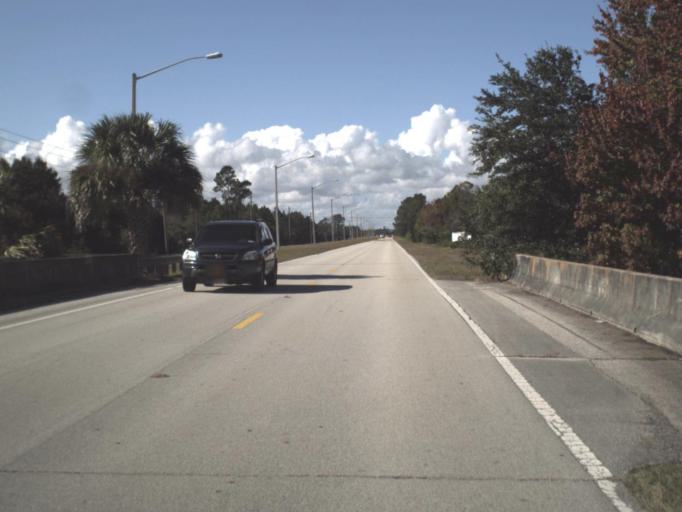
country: US
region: Florida
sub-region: Flagler County
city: Palm Coast
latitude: 29.5994
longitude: -81.2557
